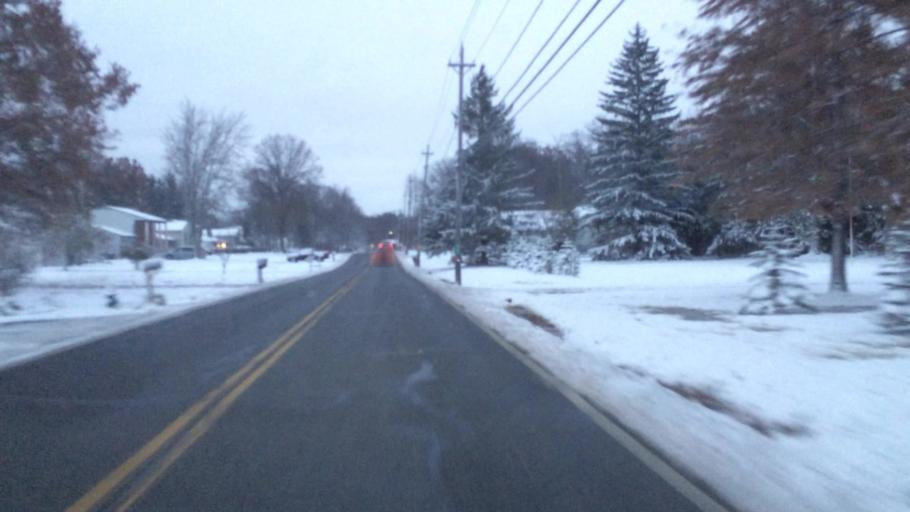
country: US
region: Ohio
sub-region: Cuyahoga County
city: Olmsted Falls
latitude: 41.3649
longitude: -81.9128
